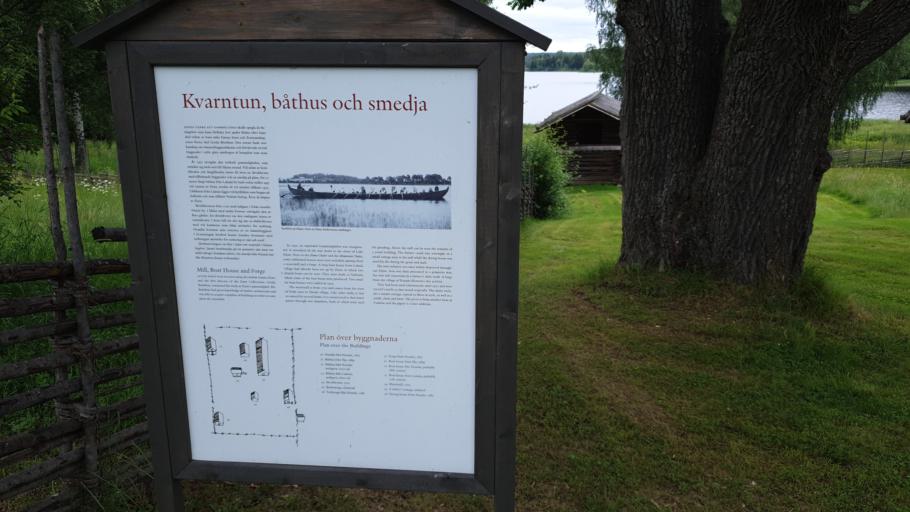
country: SE
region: Dalarna
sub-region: Mora Kommun
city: Mora
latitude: 60.9984
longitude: 14.5464
